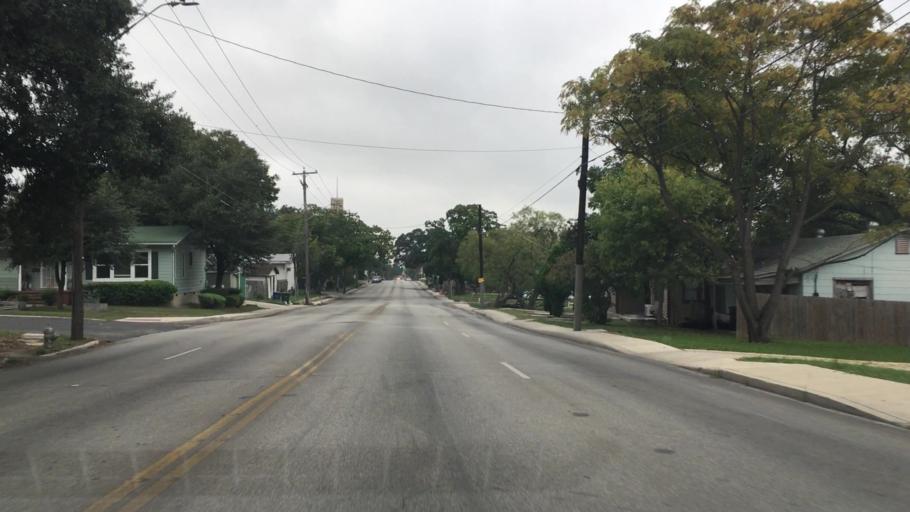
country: US
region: Texas
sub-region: Bexar County
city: Balcones Heights
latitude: 29.4726
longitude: -98.5483
